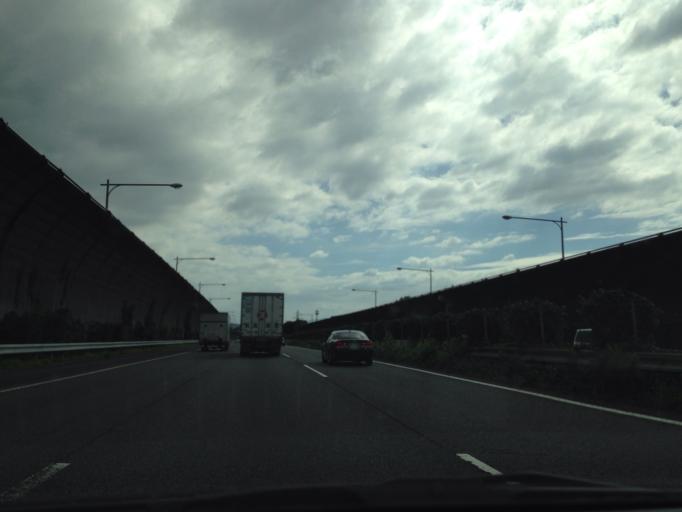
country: JP
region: Kanagawa
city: Isehara
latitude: 35.3985
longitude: 139.2866
